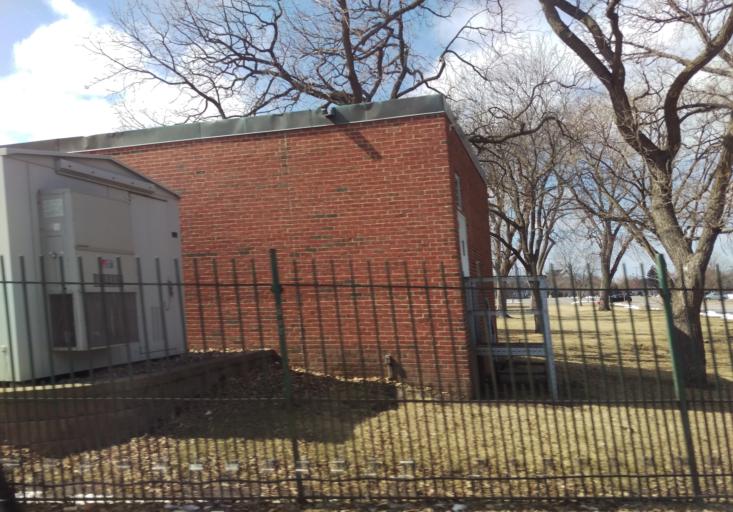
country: US
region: Minnesota
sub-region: Dakota County
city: Mendota Heights
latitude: 44.9042
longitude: -93.2029
